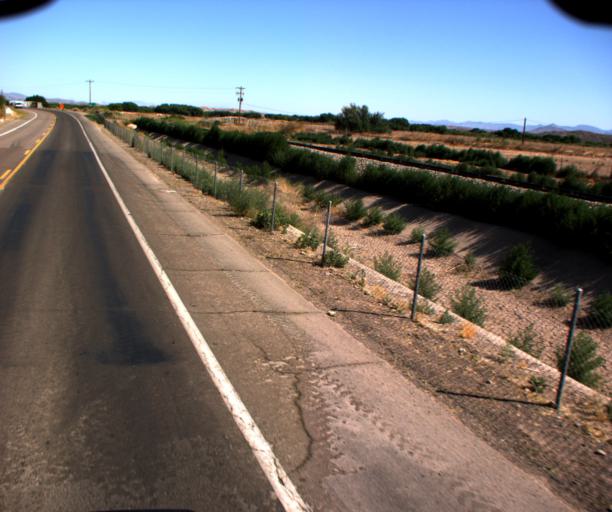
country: US
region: Arizona
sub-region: Greenlee County
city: Clifton
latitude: 32.7288
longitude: -109.1109
